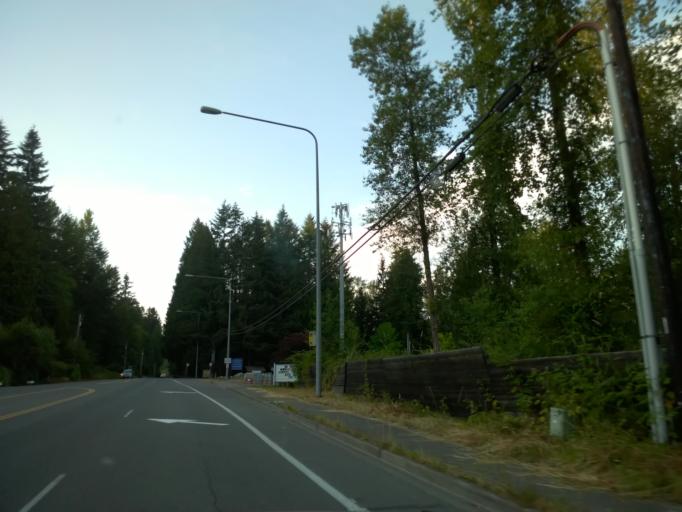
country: US
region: Washington
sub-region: King County
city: Cottage Lake
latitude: 47.7184
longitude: -122.0875
